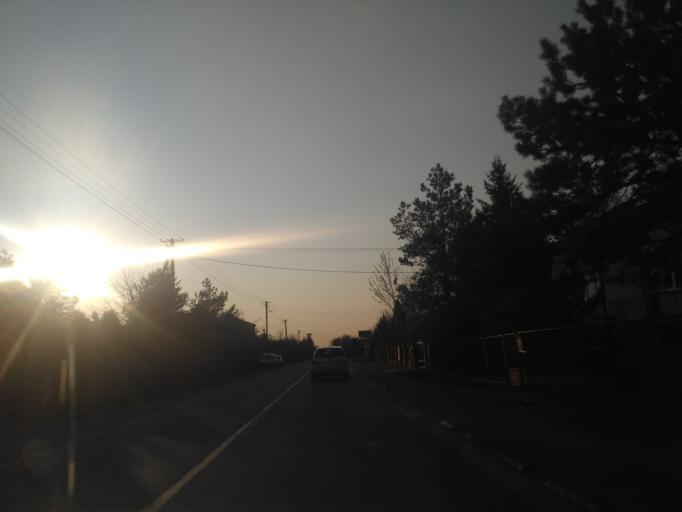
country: PL
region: Lublin Voivodeship
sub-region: Powiat chelmski
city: Pokrowka
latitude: 51.0972
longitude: 23.4884
